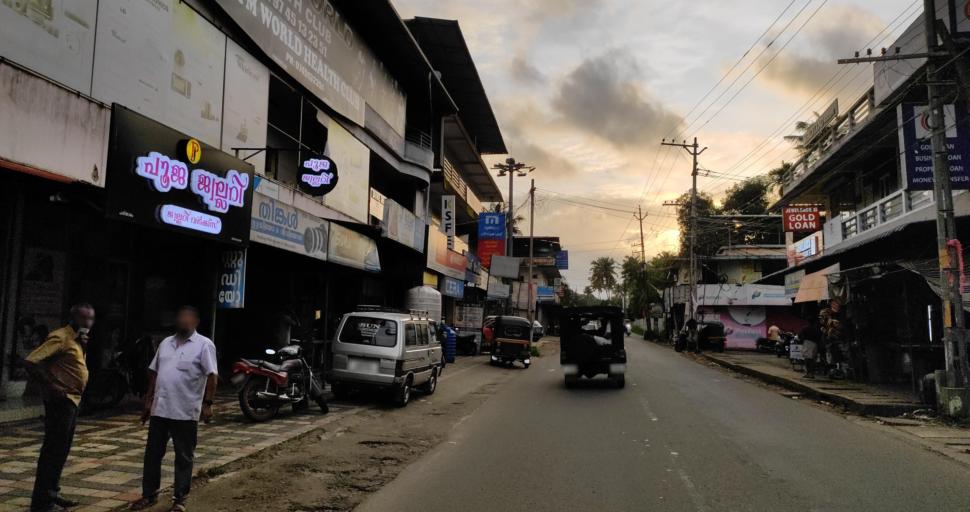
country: IN
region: Kerala
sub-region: Thrissur District
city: Kizhake Chalakudi
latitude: 10.3204
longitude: 76.3705
